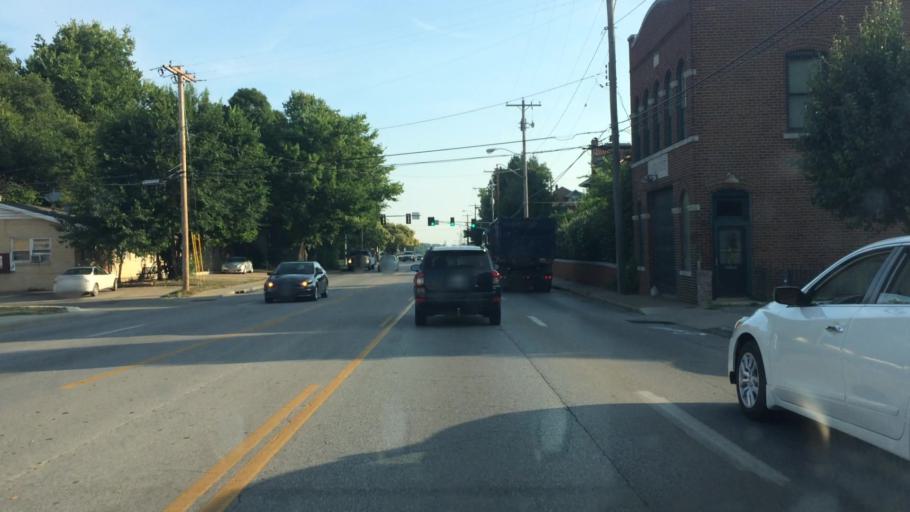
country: US
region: Missouri
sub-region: Greene County
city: Springfield
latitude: 37.2055
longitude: -93.2761
